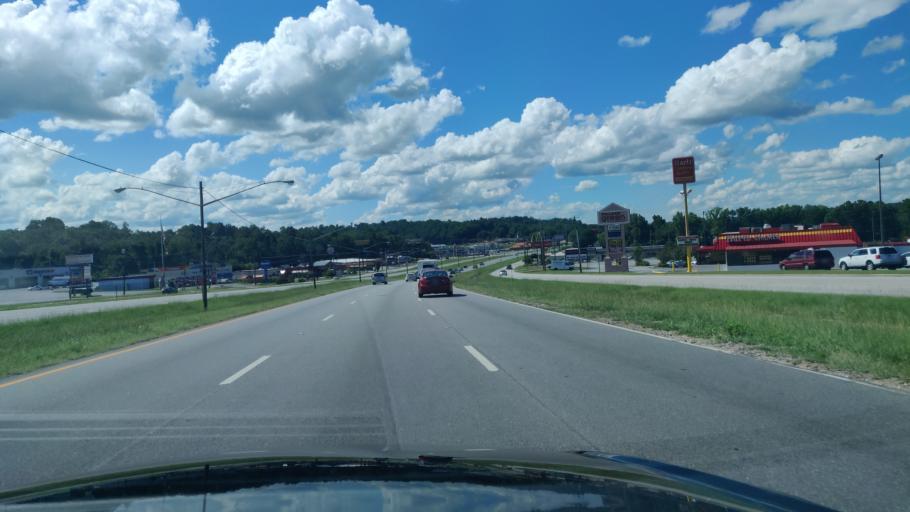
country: US
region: Alabama
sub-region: Russell County
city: Phenix City
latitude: 32.4667
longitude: -85.0271
